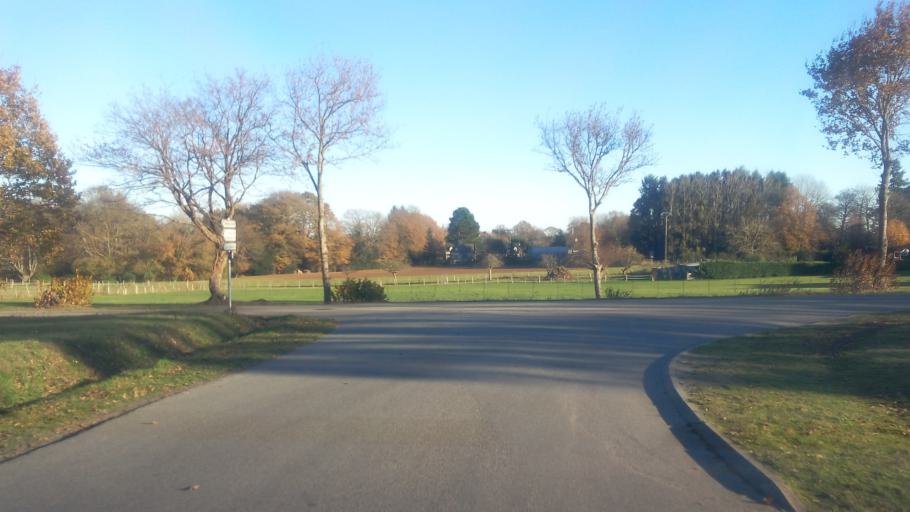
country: FR
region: Brittany
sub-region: Departement du Morbihan
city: Peillac
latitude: 47.7177
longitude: -2.2257
